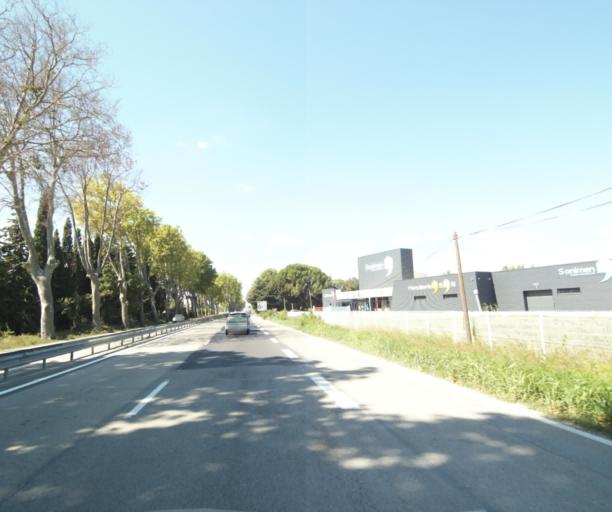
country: FR
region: Languedoc-Roussillon
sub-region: Departement du Gard
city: Rodilhan
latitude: 43.8336
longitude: 4.4215
